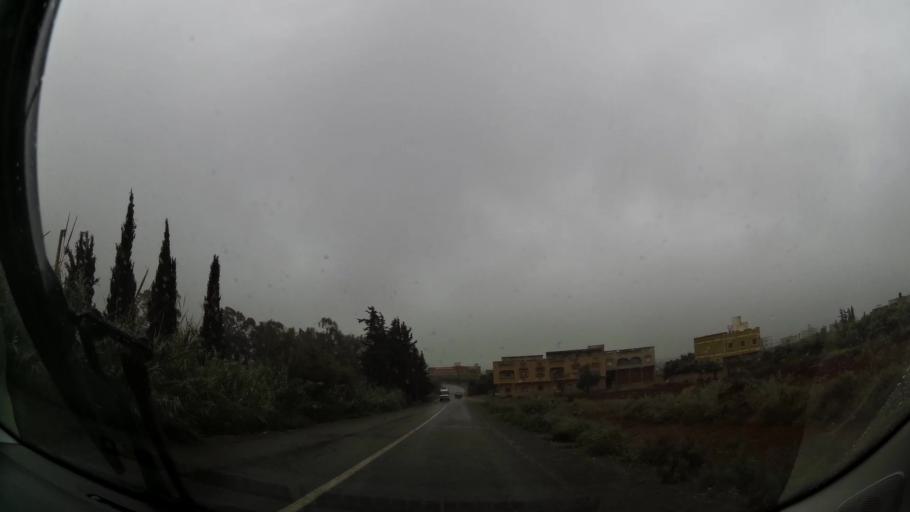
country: MA
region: Oriental
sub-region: Nador
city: Boudinar
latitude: 35.1417
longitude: -3.6158
